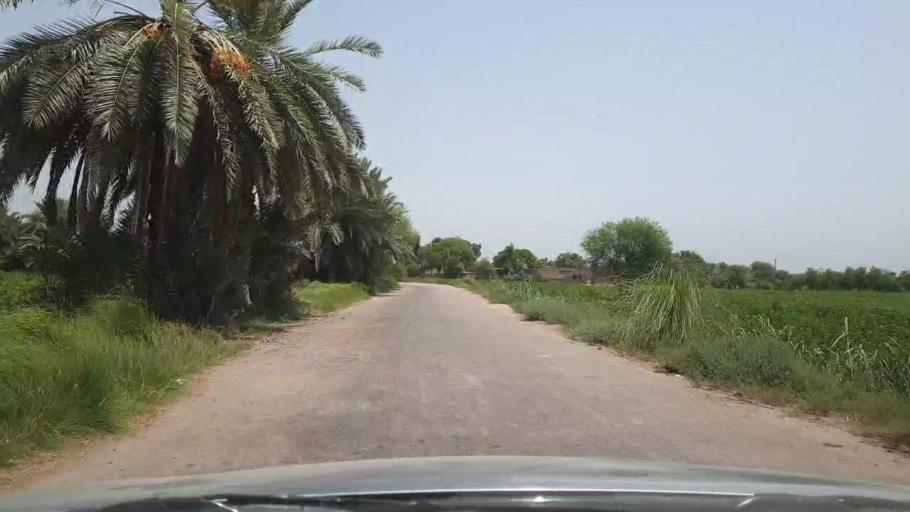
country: PK
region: Sindh
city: Pano Aqil
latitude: 27.8756
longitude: 69.1515
